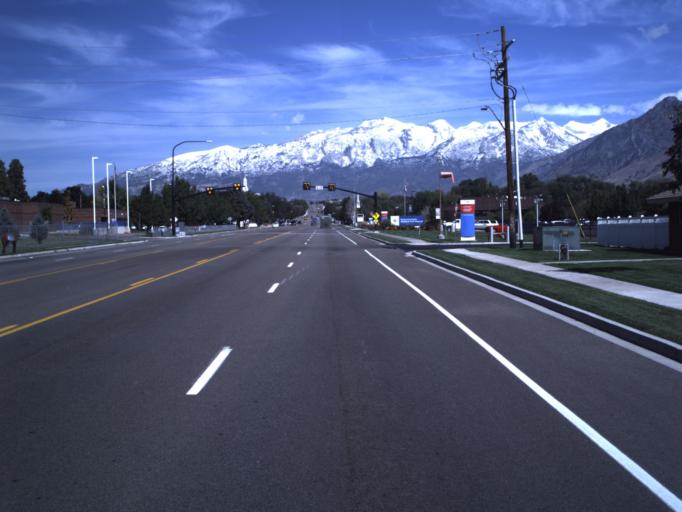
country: US
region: Utah
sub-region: Utah County
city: American Fork
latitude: 40.3790
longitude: -111.7690
